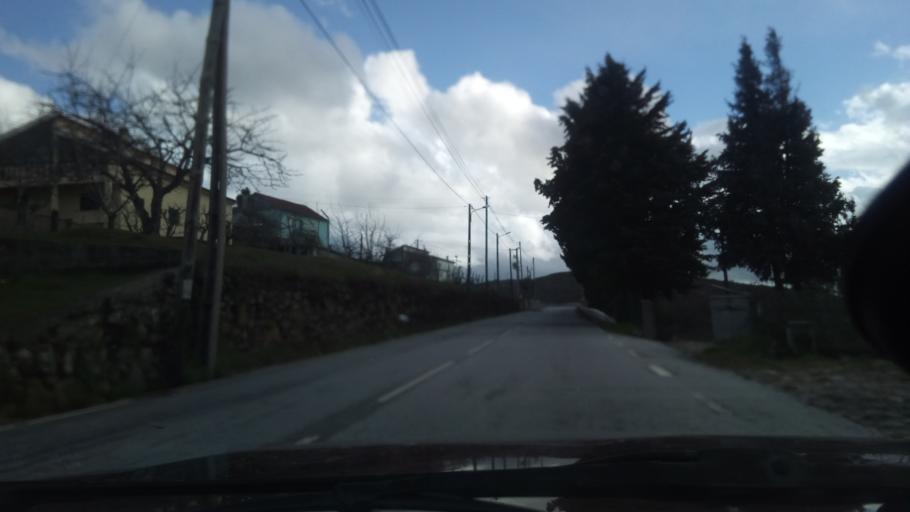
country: PT
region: Guarda
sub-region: Guarda
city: Guarda
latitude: 40.5440
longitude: -7.3176
